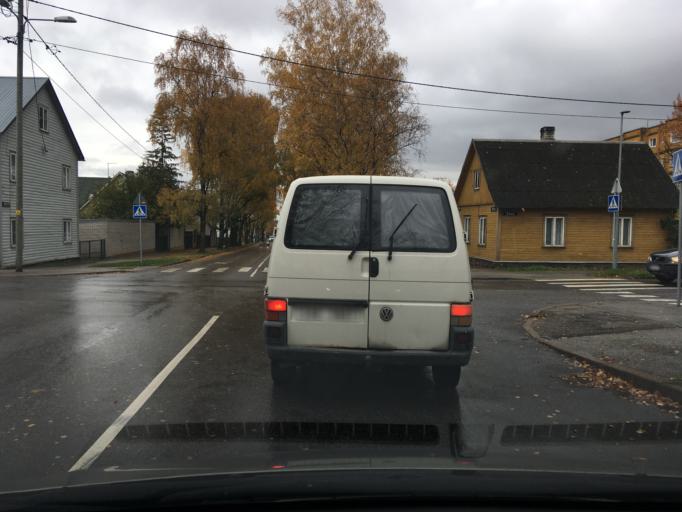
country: EE
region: Tartu
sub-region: Tartu linn
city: Tartu
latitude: 58.3646
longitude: 26.7361
